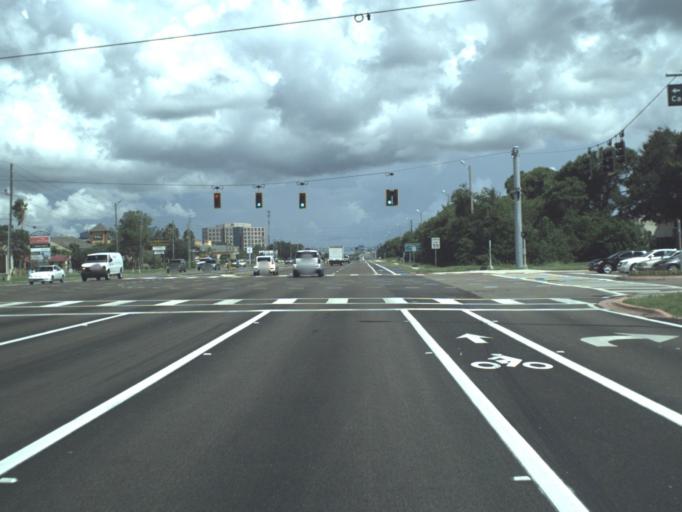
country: US
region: Florida
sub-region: Pinellas County
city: Feather Sound
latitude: 27.8937
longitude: -82.6688
